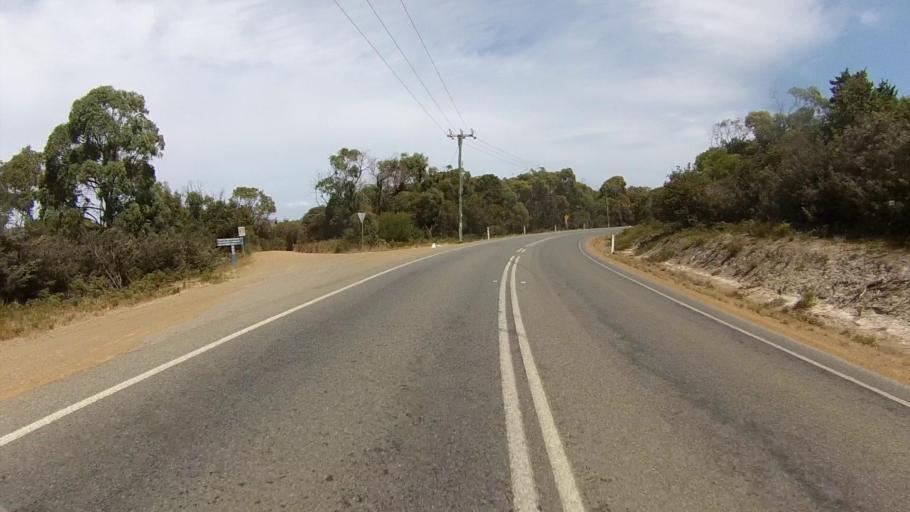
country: AU
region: Tasmania
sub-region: Clarence
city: Sandford
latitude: -43.0233
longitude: 147.4870
